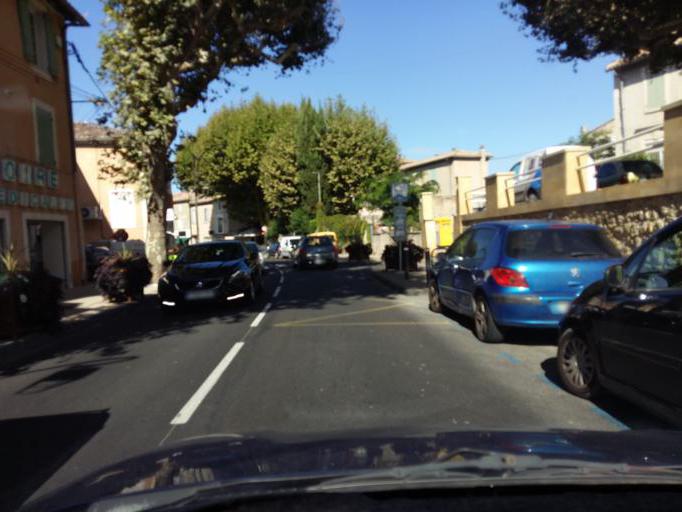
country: FR
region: Provence-Alpes-Cote d'Azur
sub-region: Departement du Vaucluse
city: Mazan
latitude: 44.0576
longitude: 5.1288
